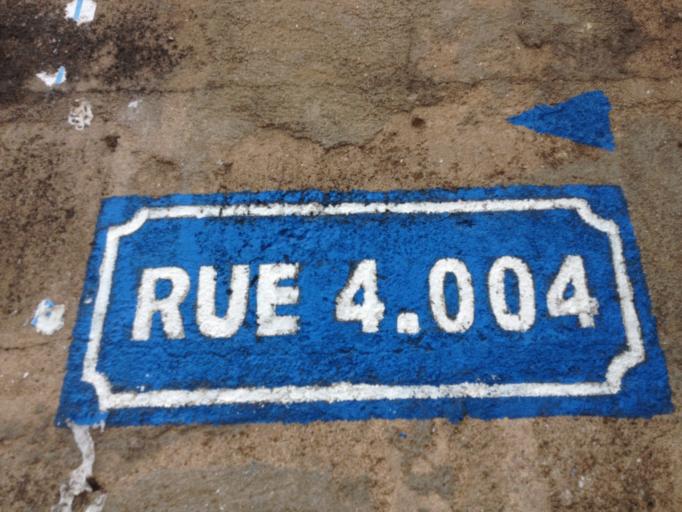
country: BJ
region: Littoral
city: Cotonou
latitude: 6.3584
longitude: 2.4467
